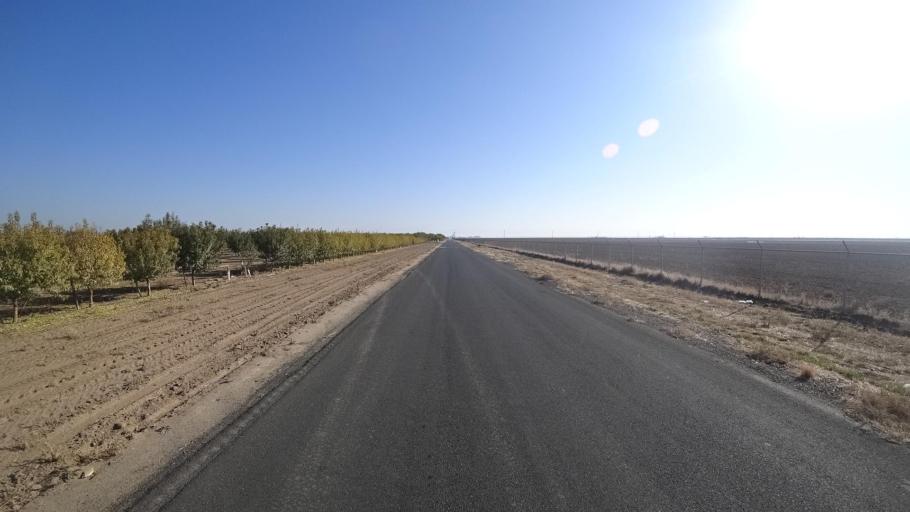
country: US
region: California
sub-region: Kern County
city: Delano
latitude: 35.7470
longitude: -119.2298
